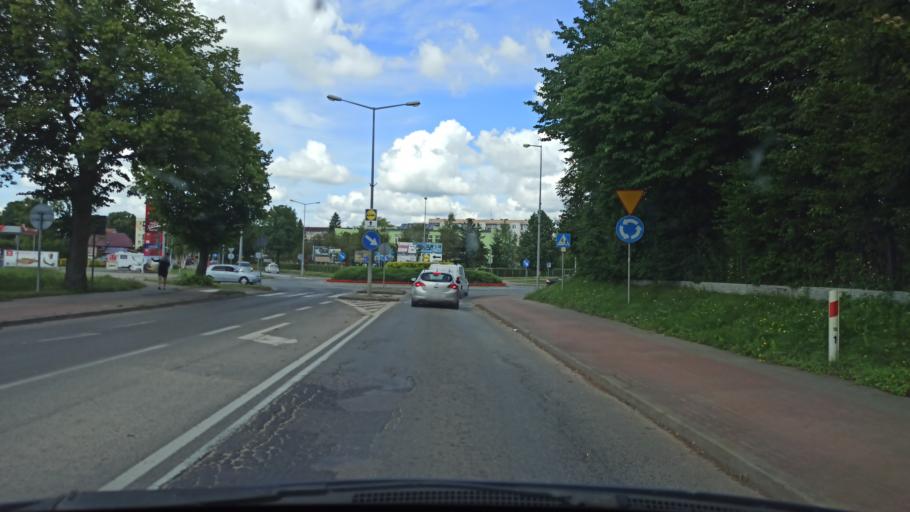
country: PL
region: Warmian-Masurian Voivodeship
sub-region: Powiat ostrodzki
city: Morag
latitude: 53.9070
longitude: 19.9364
